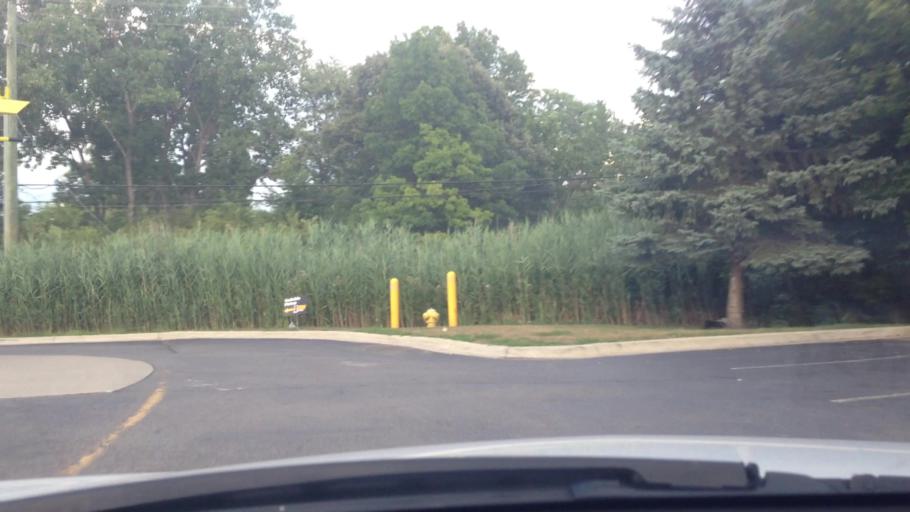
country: US
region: Michigan
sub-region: Wayne County
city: Woodhaven
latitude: 42.1663
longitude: -83.2658
